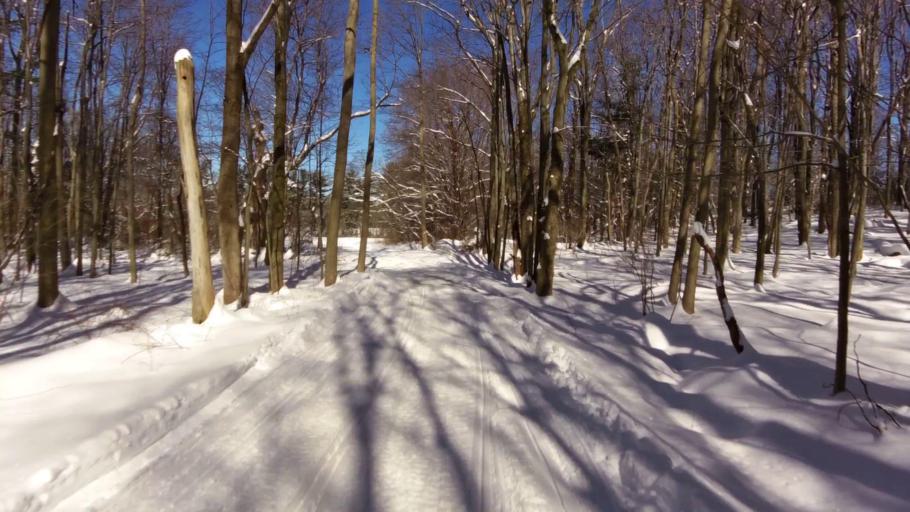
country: US
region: New York
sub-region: Chautauqua County
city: Mayville
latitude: 42.2359
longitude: -79.4204
